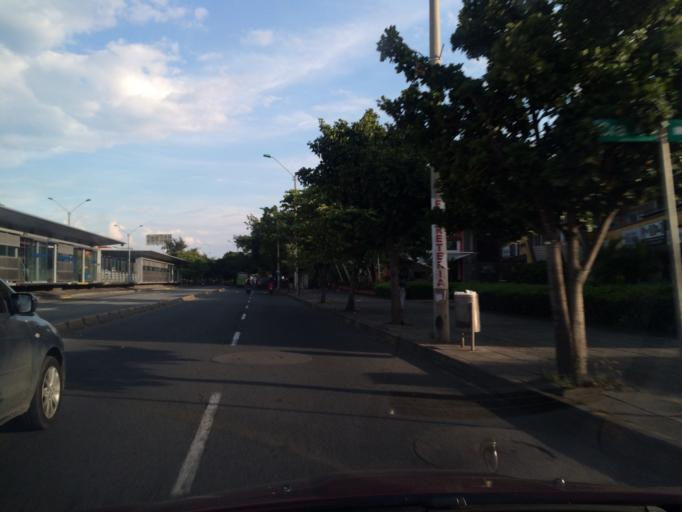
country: CO
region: Valle del Cauca
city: Cali
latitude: 3.4195
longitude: -76.5484
